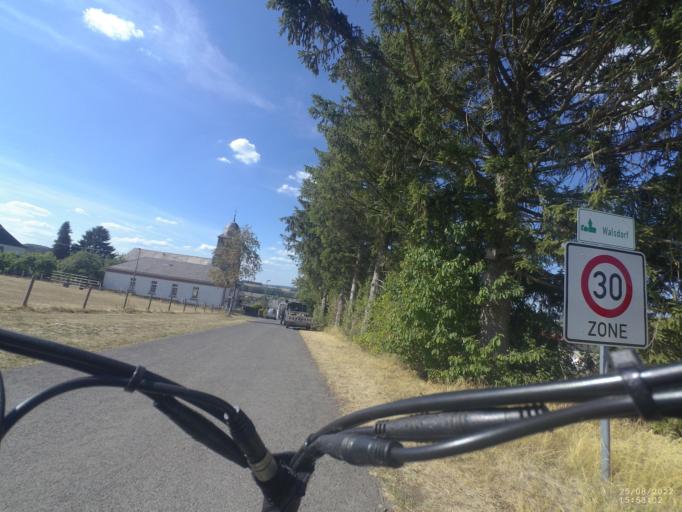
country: DE
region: Rheinland-Pfalz
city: Walsdorf
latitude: 50.2789
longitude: 6.7153
